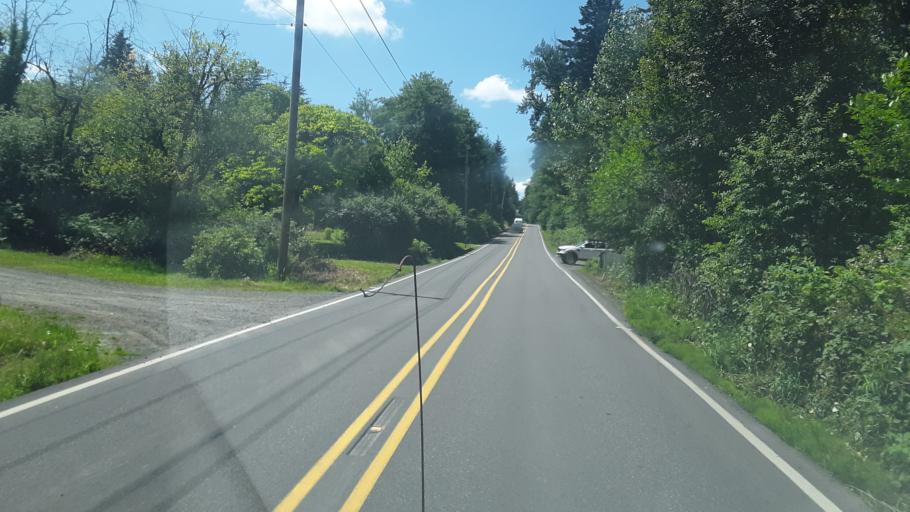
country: US
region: Washington
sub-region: Clark County
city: Amboy
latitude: 45.8957
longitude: -122.4558
